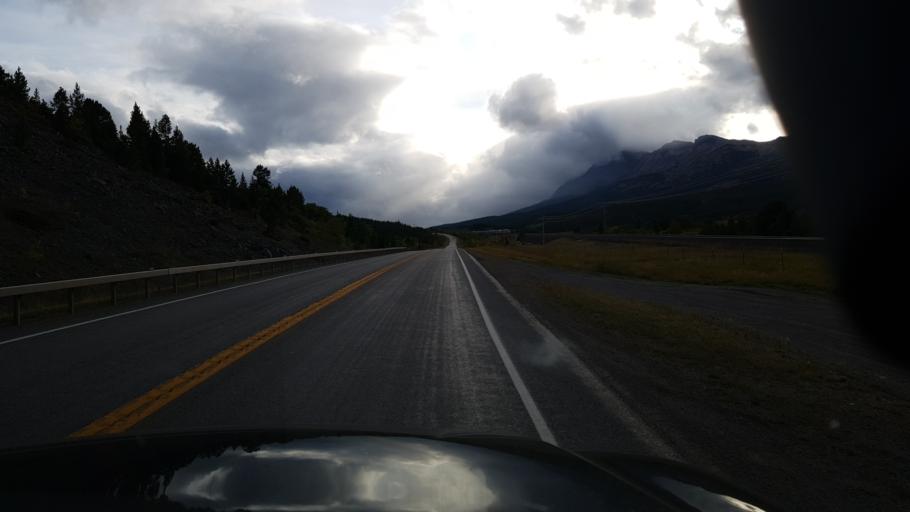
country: US
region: Montana
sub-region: Glacier County
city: South Browning
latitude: 48.3899
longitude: -113.2601
